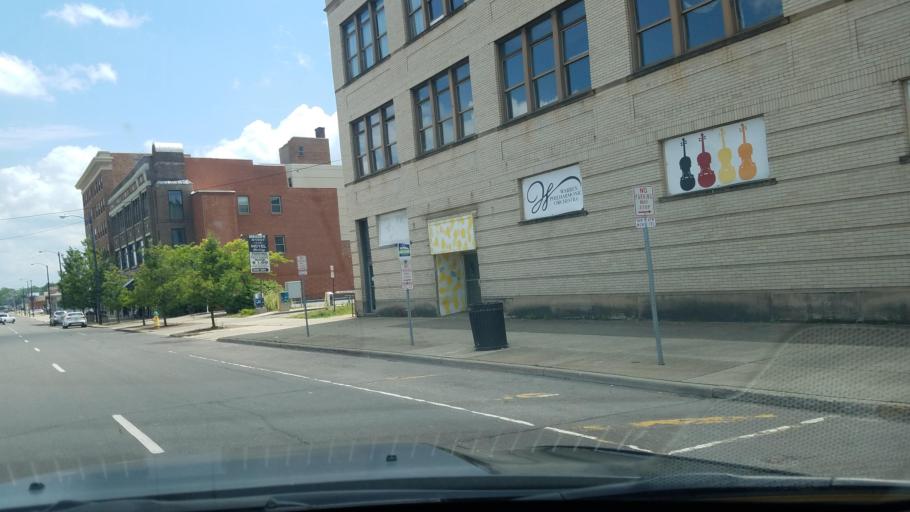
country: US
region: Ohio
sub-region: Trumbull County
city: Warren
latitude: 41.2374
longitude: -80.8179
